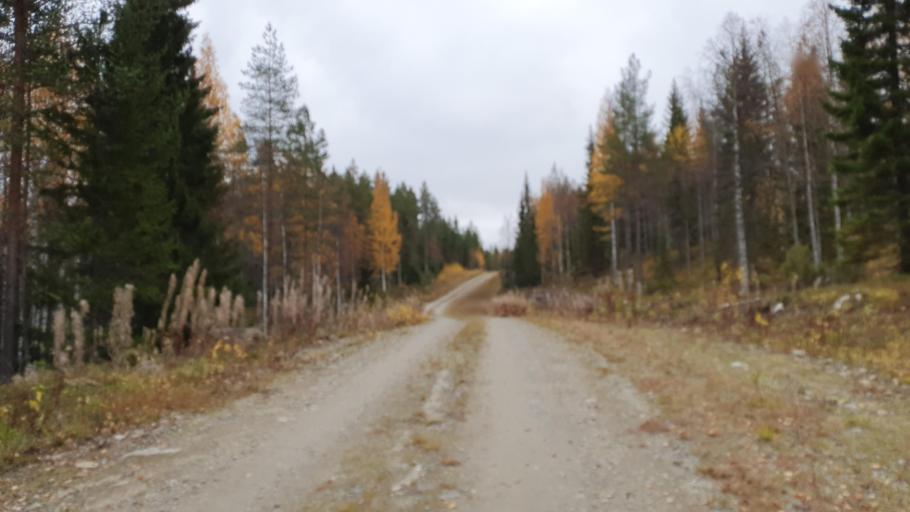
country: FI
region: Kainuu
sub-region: Kehys-Kainuu
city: Kuhmo
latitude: 64.4458
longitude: 29.6239
